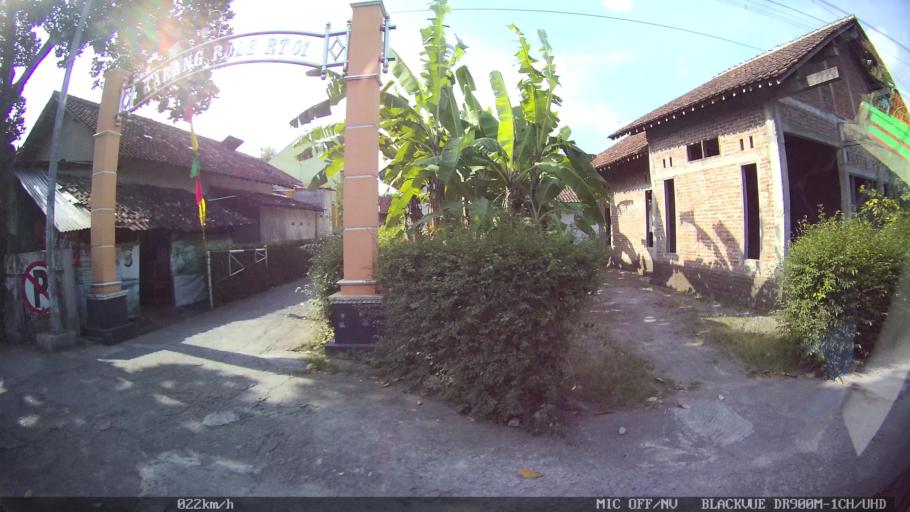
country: ID
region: Daerah Istimewa Yogyakarta
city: Kasihan
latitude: -7.8461
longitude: 110.3390
